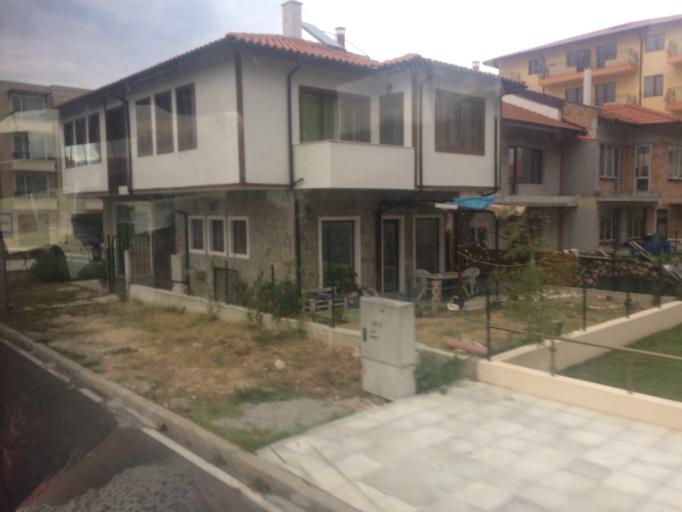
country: BG
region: Burgas
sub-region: Obshtina Nesebur
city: Ravda
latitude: 42.6596
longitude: 27.7022
